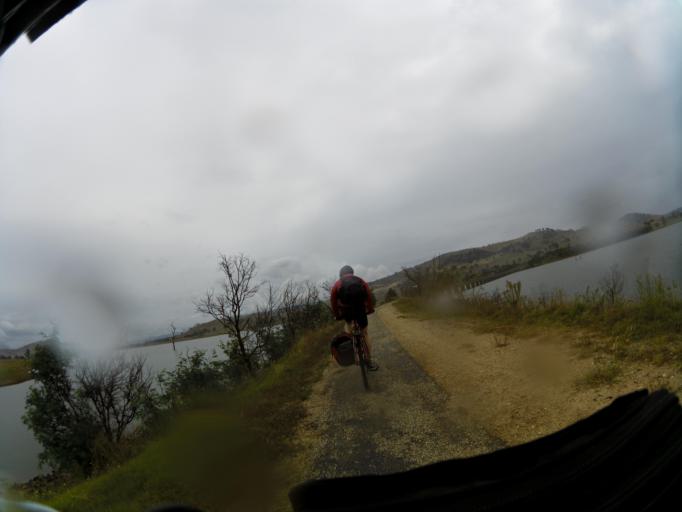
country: AU
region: New South Wales
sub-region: Albury Municipality
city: East Albury
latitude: -36.2359
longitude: 147.0925
